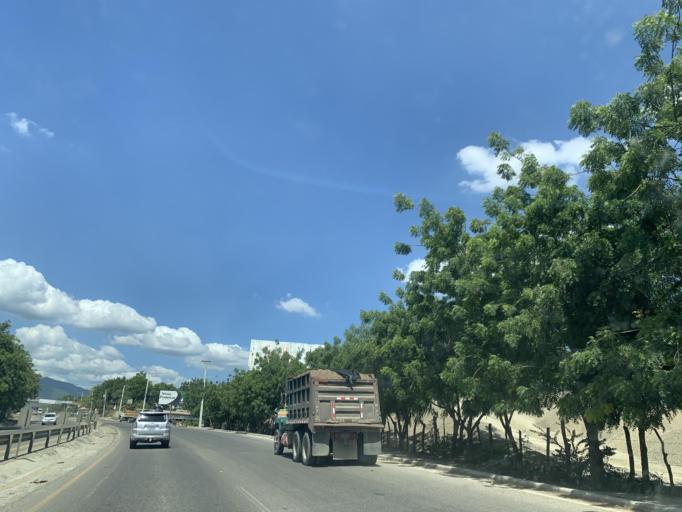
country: DO
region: Santiago
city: Villa Bisono
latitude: 19.5479
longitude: -70.8498
